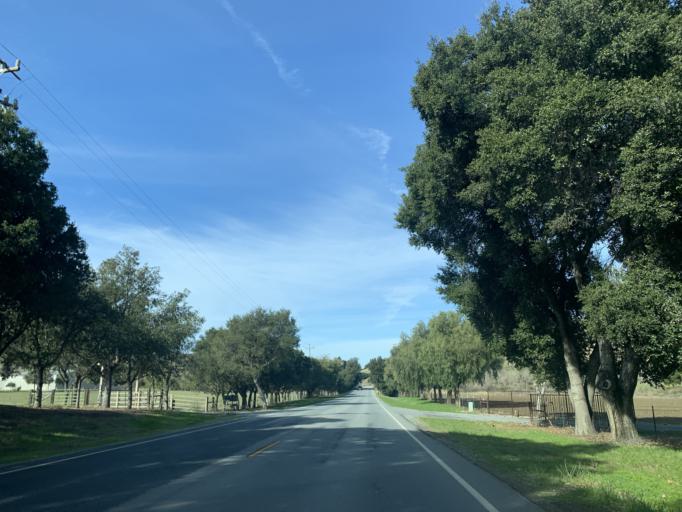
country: US
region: California
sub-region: San Benito County
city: Ridgemark
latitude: 36.7624
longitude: -121.2973
